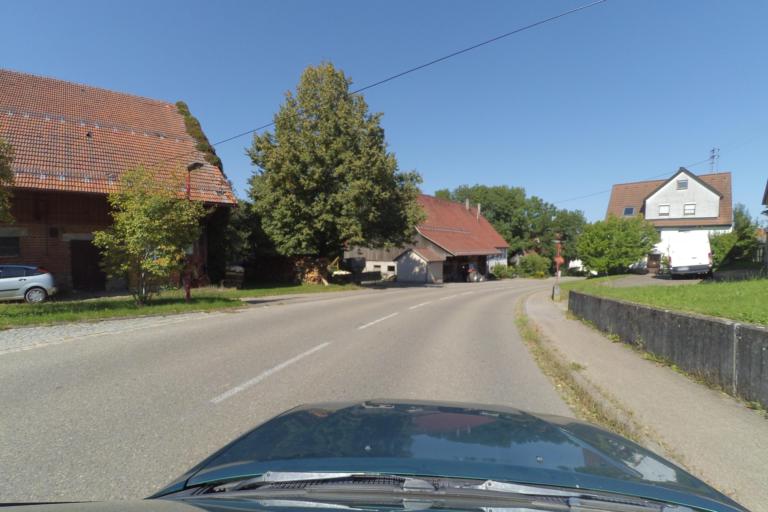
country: DE
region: Baden-Wuerttemberg
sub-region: Regierungsbezirk Stuttgart
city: Ruppertshofen
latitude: 48.8819
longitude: 9.8139
